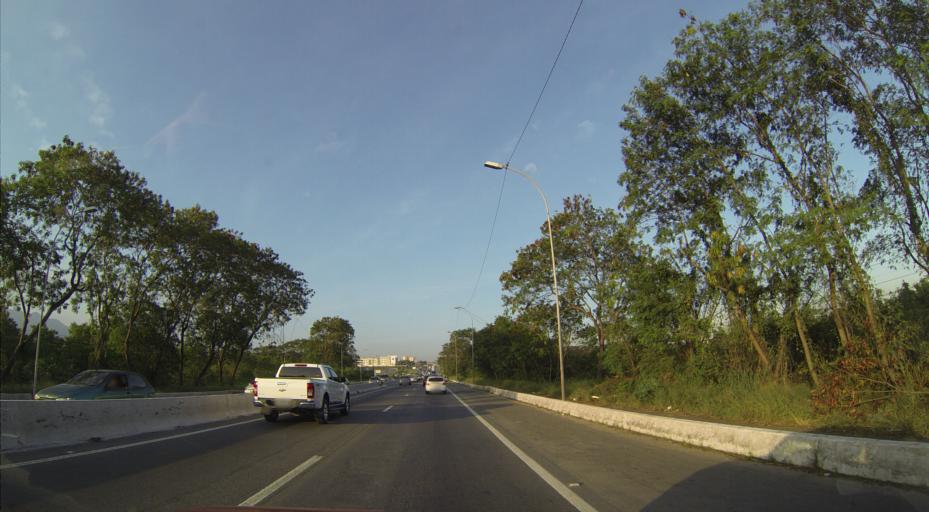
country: BR
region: Espirito Santo
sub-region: Vila Velha
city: Vila Velha
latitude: -20.2434
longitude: -40.2816
